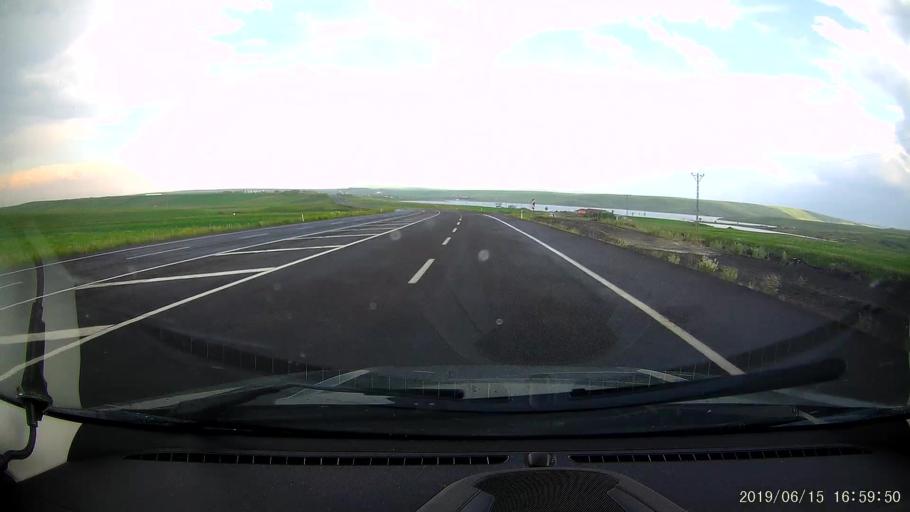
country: TR
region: Kars
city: Susuz
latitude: 40.7465
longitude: 43.1537
